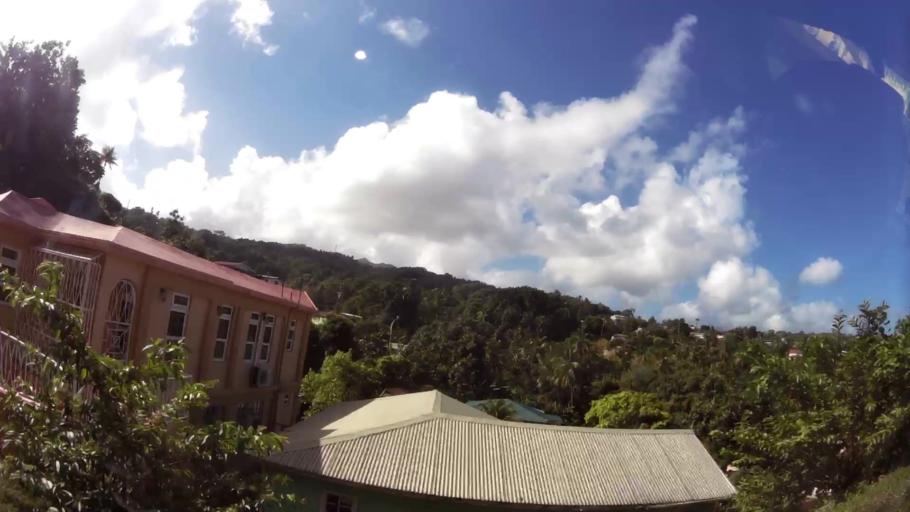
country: DM
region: Saint Andrew
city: Marigot
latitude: 15.5401
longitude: -61.2846
